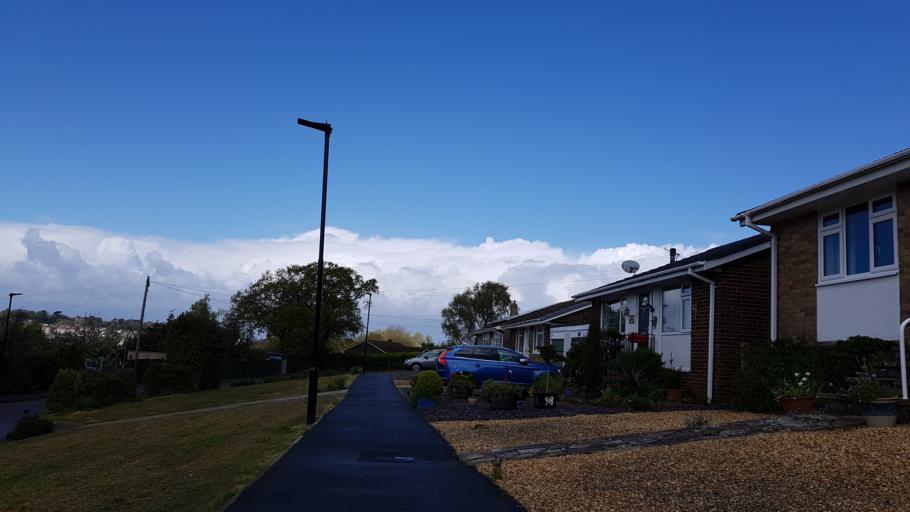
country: GB
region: England
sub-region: Isle of Wight
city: East Cowes
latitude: 50.7569
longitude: -1.2817
